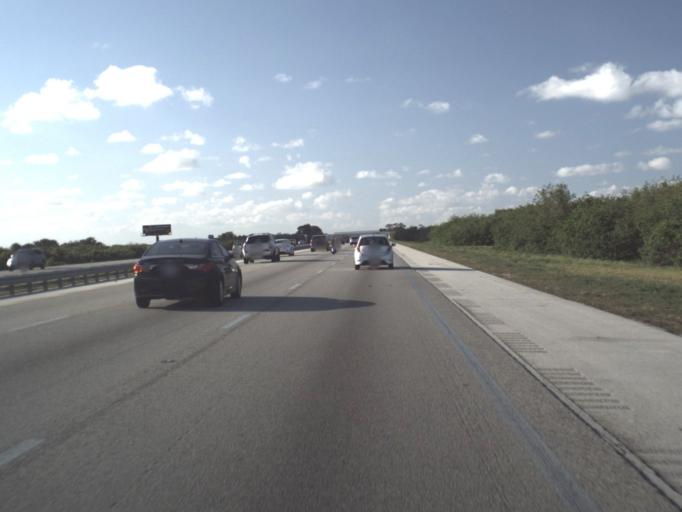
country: US
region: Florida
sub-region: Brevard County
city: Rockledge
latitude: 28.2561
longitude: -80.7258
